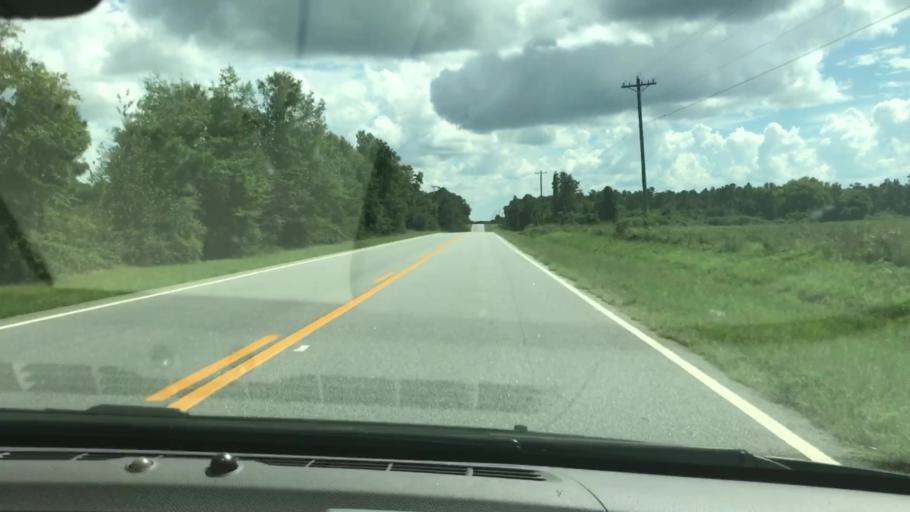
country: US
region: Georgia
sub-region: Quitman County
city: Georgetown
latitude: 31.7943
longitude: -85.0924
